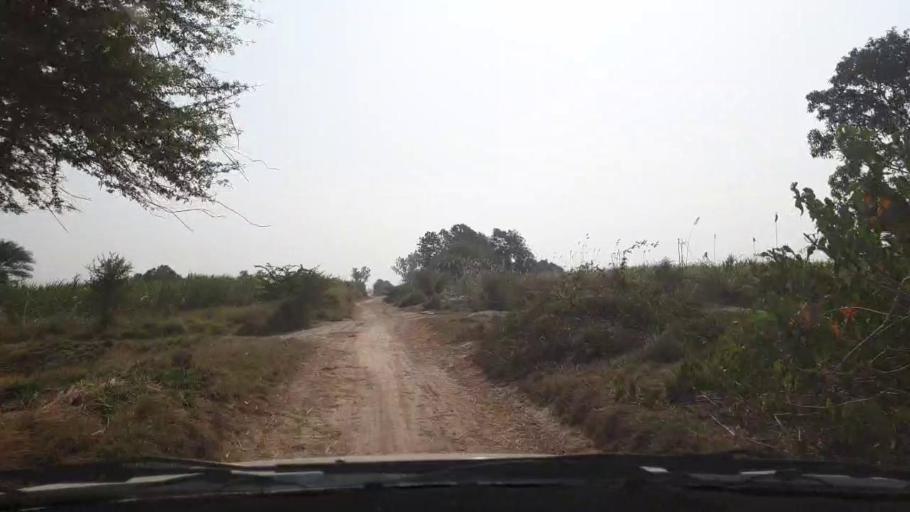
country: PK
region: Sindh
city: Tando Muhammad Khan
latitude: 25.0788
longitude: 68.3616
